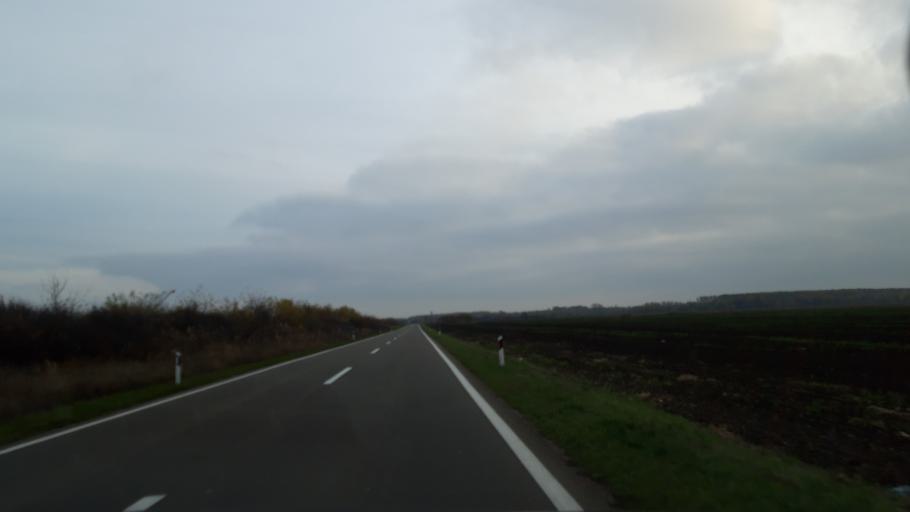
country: RS
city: Sanad
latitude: 46.0046
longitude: 20.1011
